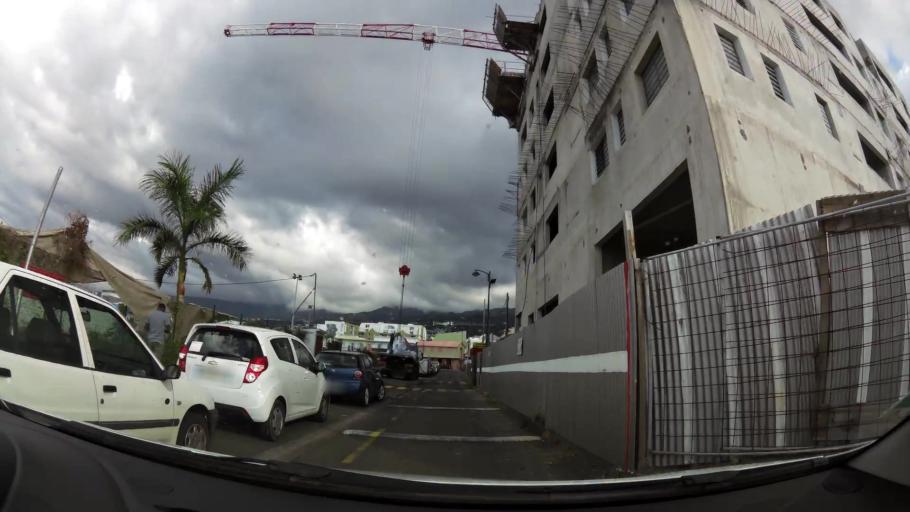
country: RE
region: Reunion
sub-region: Reunion
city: Saint-Denis
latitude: -20.8790
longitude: 55.4564
